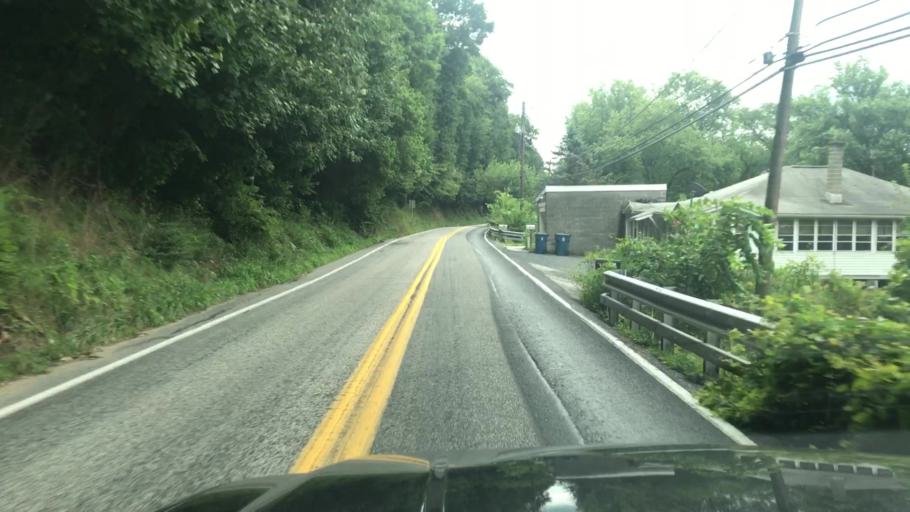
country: US
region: Pennsylvania
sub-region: Cumberland County
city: Shiremanstown
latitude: 40.2501
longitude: -76.9733
